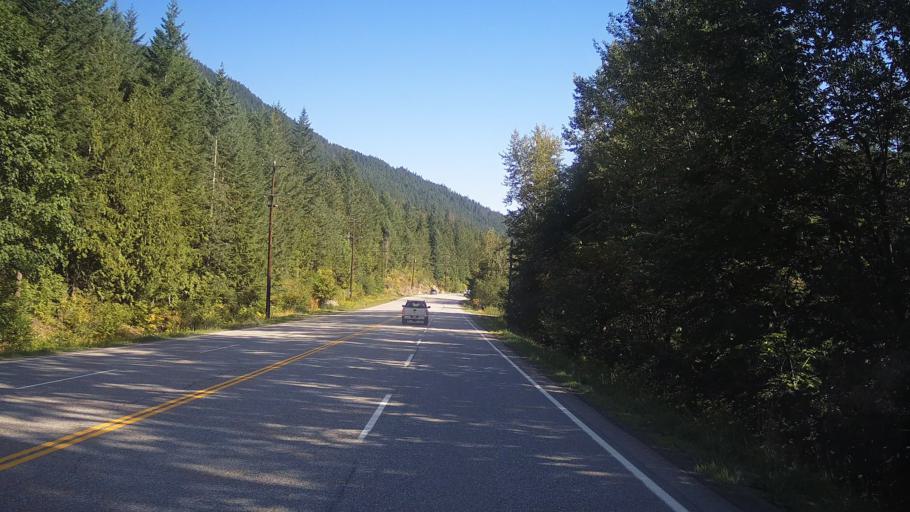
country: CA
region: British Columbia
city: Hope
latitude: 49.6734
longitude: -121.4185
